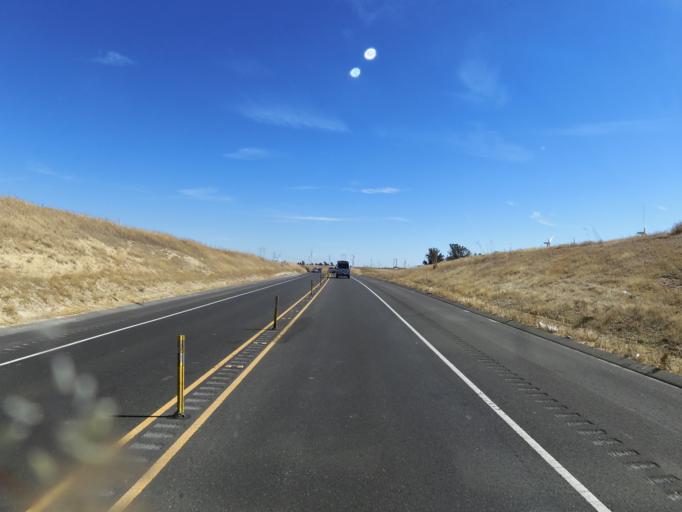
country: US
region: California
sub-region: Contra Costa County
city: Pittsburg
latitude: 38.1943
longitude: -121.8630
